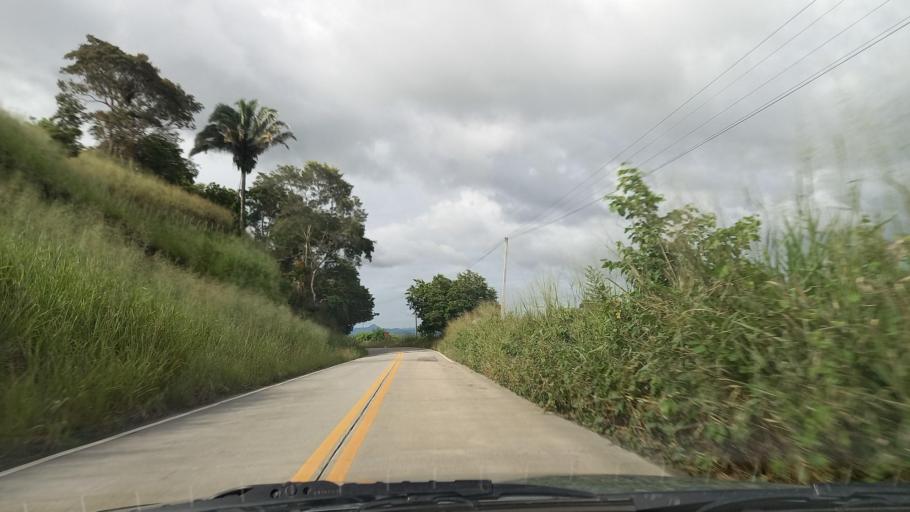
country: BR
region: Pernambuco
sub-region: Maraial
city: Maraial
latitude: -8.7875
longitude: -35.8789
